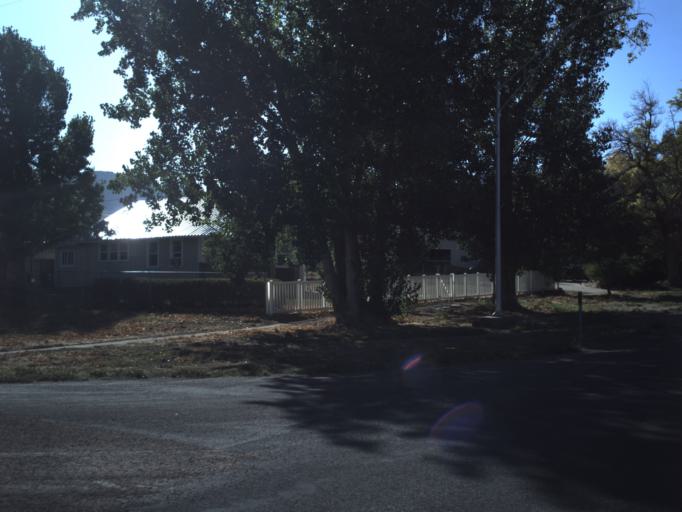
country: US
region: Utah
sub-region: Millard County
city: Delta
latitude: 39.3772
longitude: -112.3361
